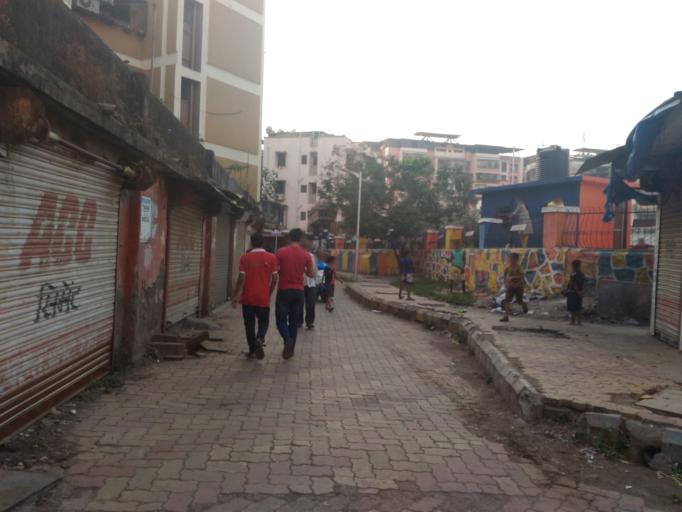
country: IN
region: Maharashtra
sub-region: Thane
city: Bhayandar
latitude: 19.3133
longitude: 72.8559
